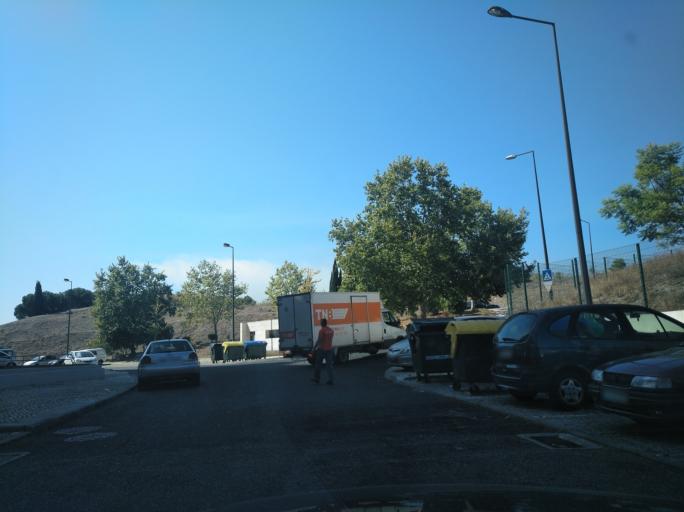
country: PT
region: Lisbon
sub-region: Lisbon
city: Lisbon
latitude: 38.7456
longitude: -9.1213
